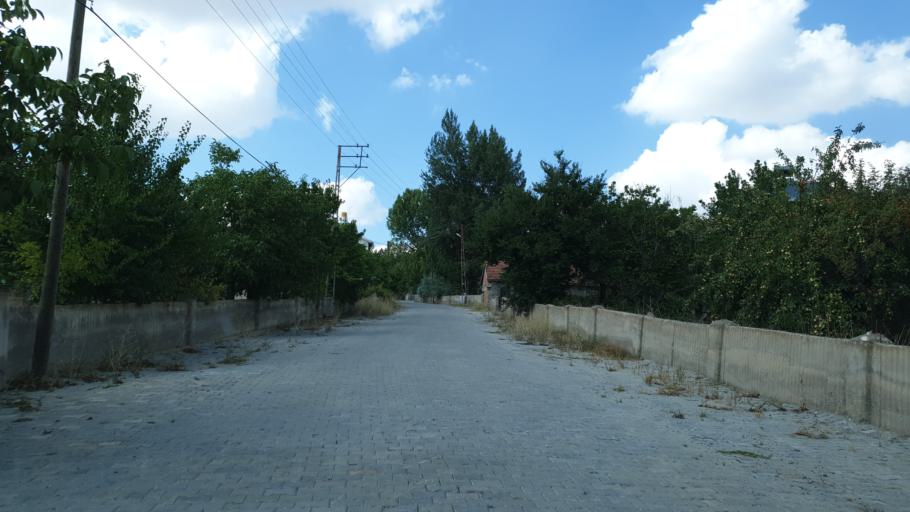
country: TR
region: Kayseri
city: Felahiye
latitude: 39.1141
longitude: 35.6102
